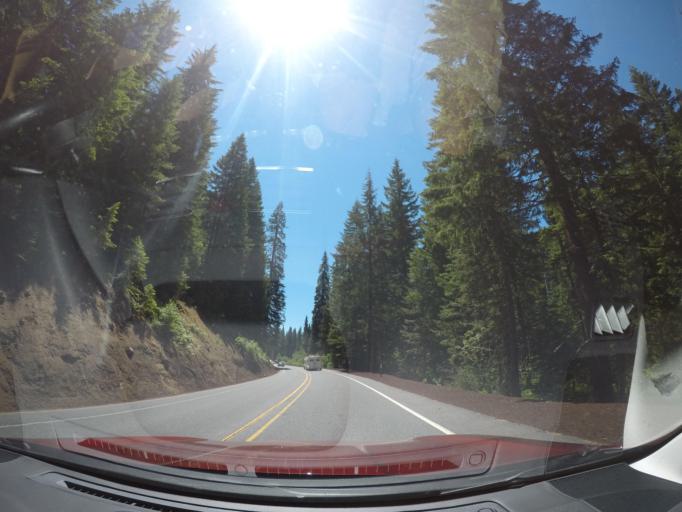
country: US
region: Oregon
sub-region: Deschutes County
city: Sisters
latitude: 44.5427
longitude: -121.9962
